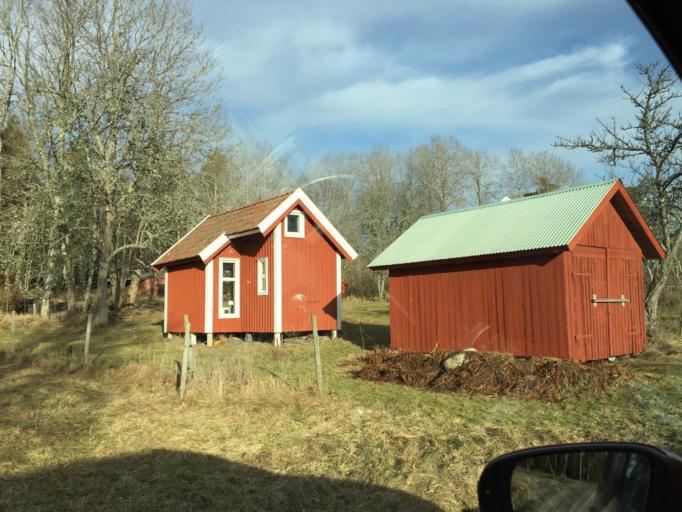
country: SE
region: OErebro
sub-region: Orebro Kommun
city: Odensbacken
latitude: 59.1013
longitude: 15.5505
